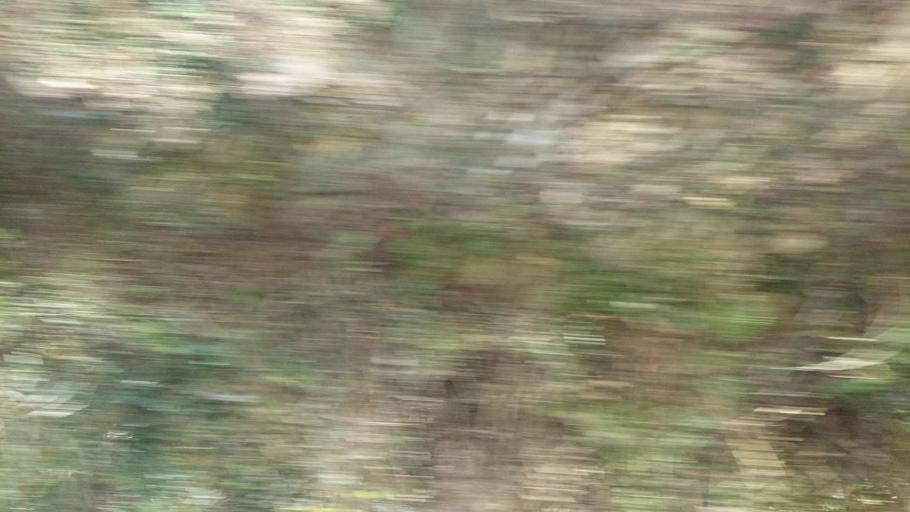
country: TW
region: Taiwan
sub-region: Hualien
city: Hualian
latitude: 24.3736
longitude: 121.3366
